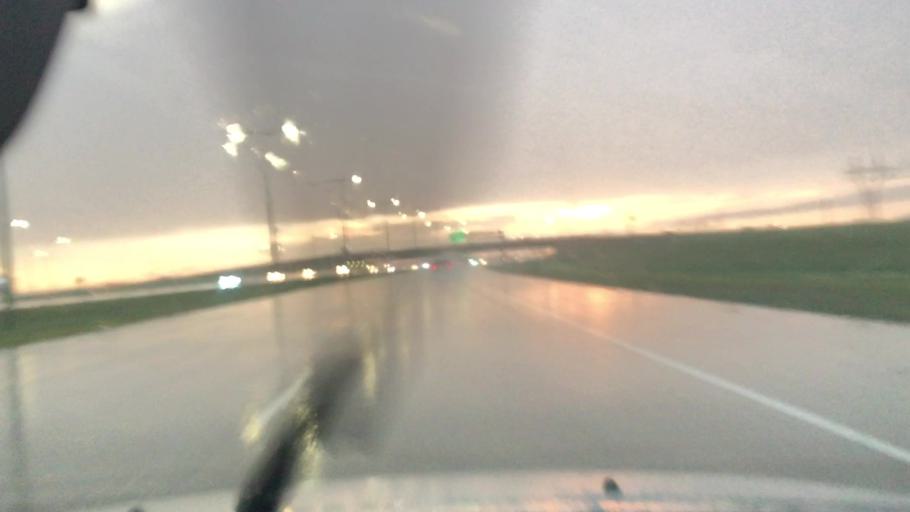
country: CA
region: Alberta
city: Edmonton
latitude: 53.4294
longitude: -113.5768
